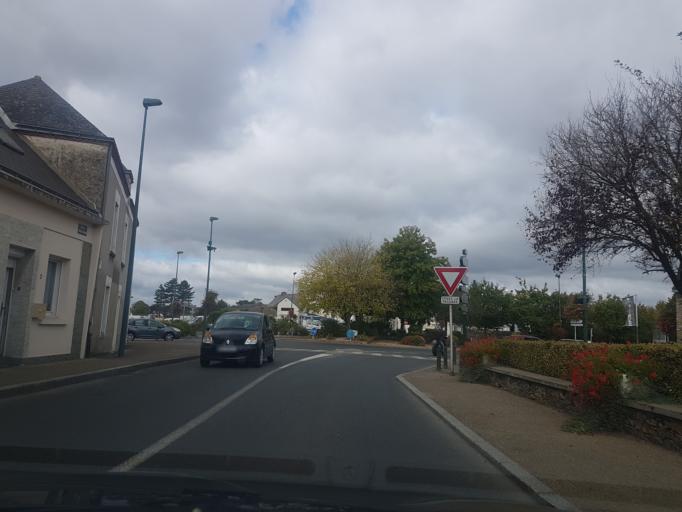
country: FR
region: Pays de la Loire
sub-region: Departement de la Loire-Atlantique
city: Ligne
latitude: 47.4108
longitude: -1.3752
